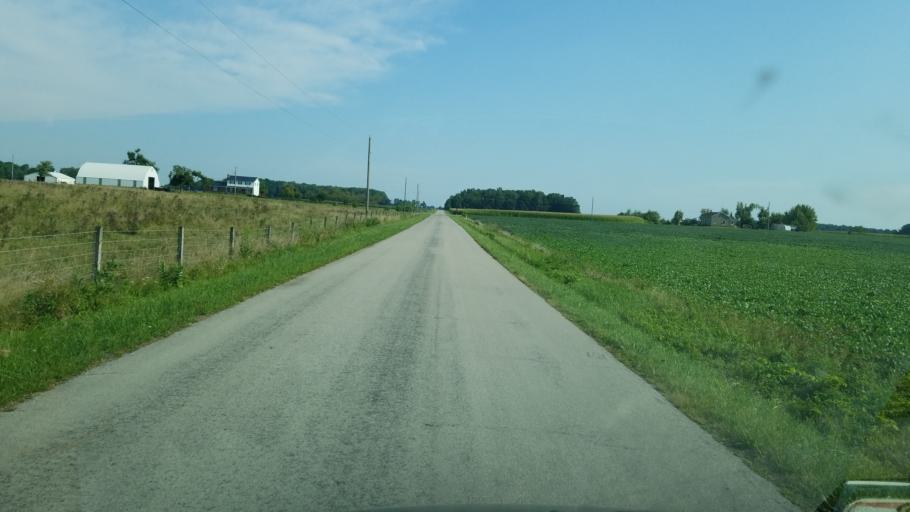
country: US
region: Ohio
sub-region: Crawford County
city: Crestline
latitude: 40.8042
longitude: -82.7645
